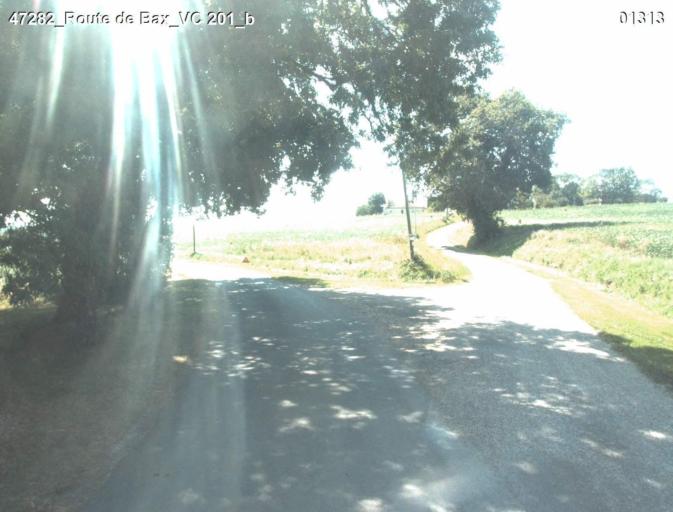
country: FR
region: Aquitaine
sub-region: Departement du Lot-et-Garonne
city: Laplume
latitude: 44.0798
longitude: 0.4956
